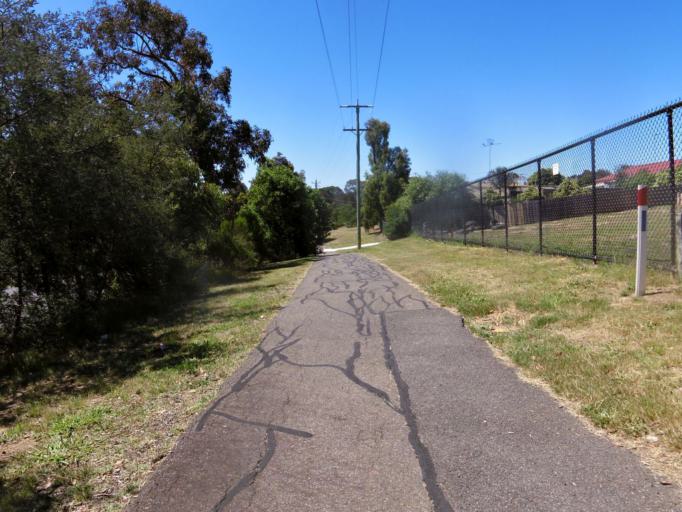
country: AU
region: Victoria
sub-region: Whittlesea
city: Whittlesea
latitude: -37.3595
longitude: 145.0275
